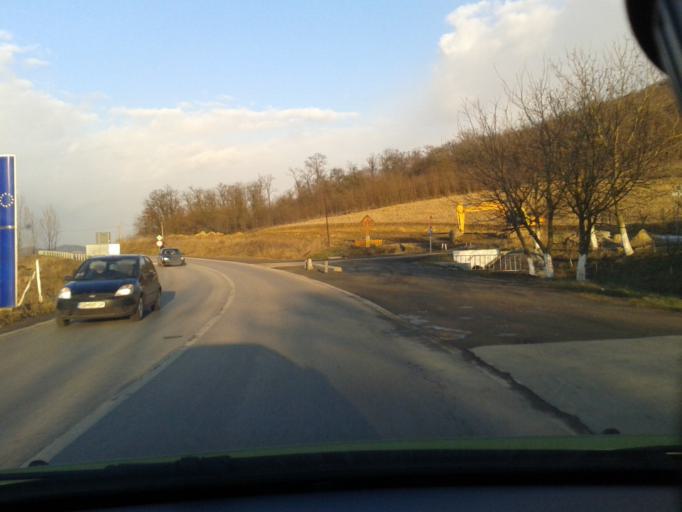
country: RO
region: Sibiu
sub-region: Comuna Tarnava
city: Tarnava
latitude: 46.1376
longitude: 24.3104
